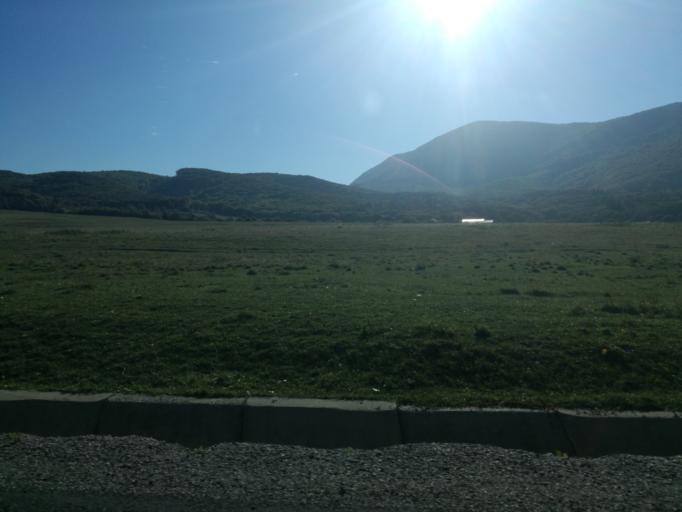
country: RO
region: Brasov
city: Codlea
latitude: 45.7325
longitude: 25.4416
